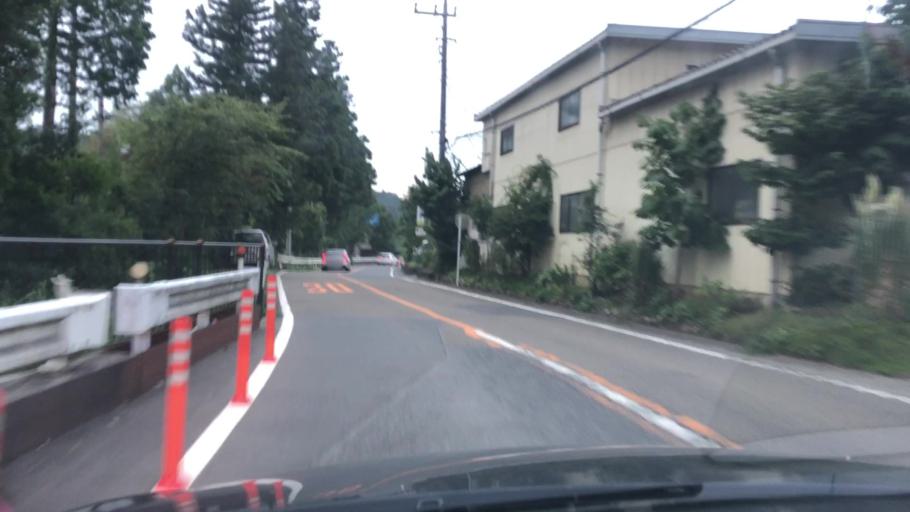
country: JP
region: Tokyo
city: Ome
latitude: 35.7521
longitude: 139.2392
